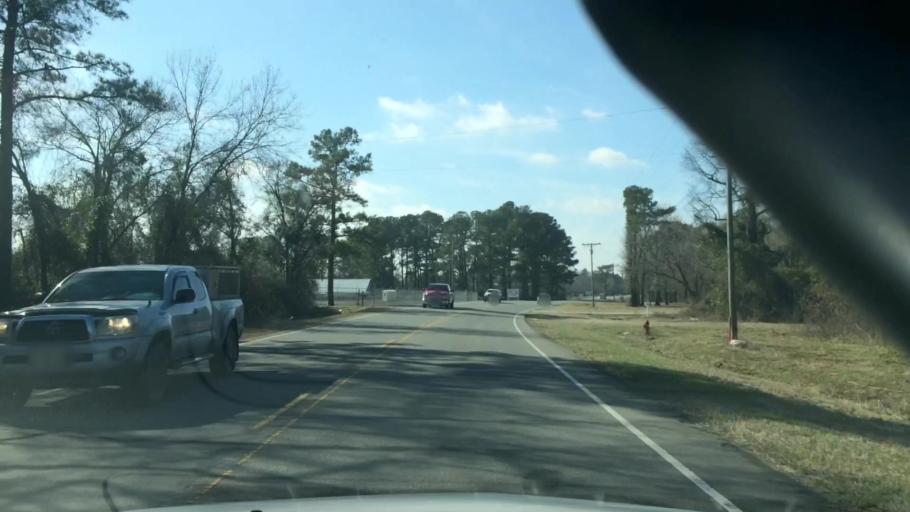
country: US
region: North Carolina
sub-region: Duplin County
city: Wallace
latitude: 34.7929
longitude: -77.8673
